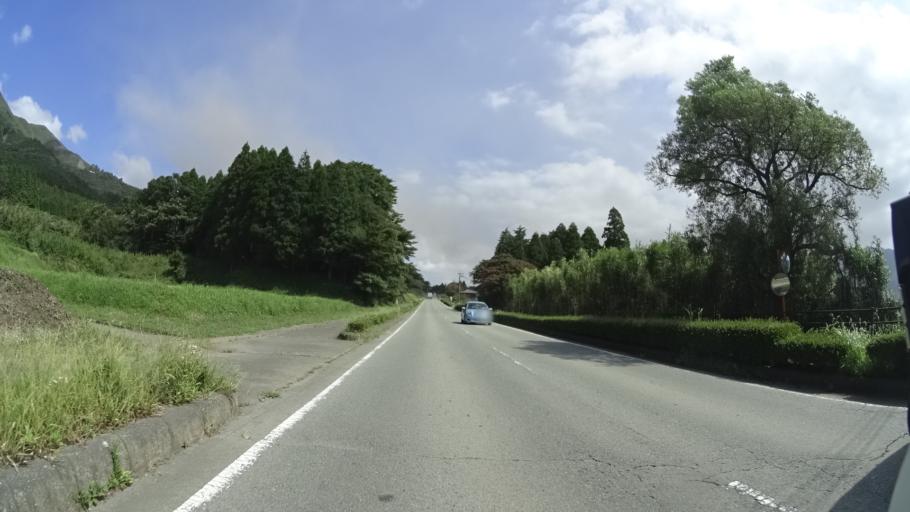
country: JP
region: Kumamoto
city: Aso
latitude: 32.8466
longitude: 131.0331
